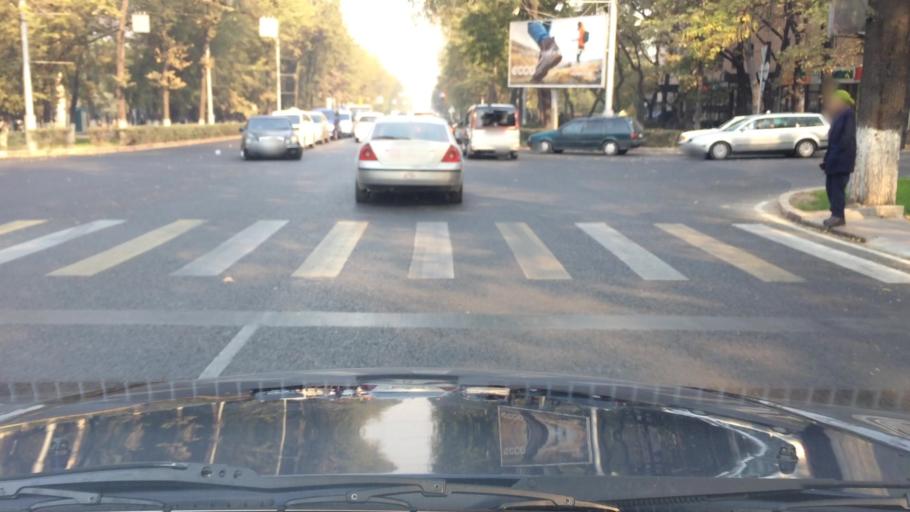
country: KG
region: Chuy
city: Bishkek
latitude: 42.8494
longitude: 74.5864
